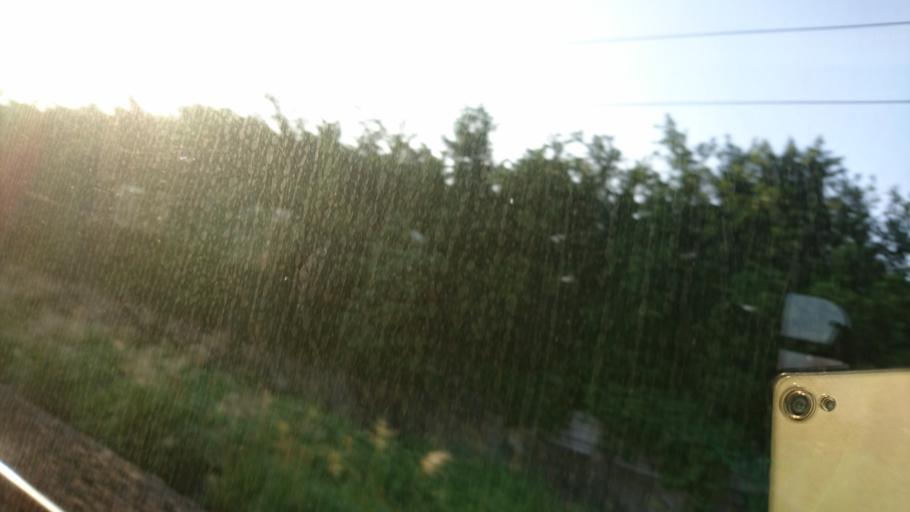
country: TW
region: Taiwan
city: Daxi
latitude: 24.9378
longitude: 121.2092
